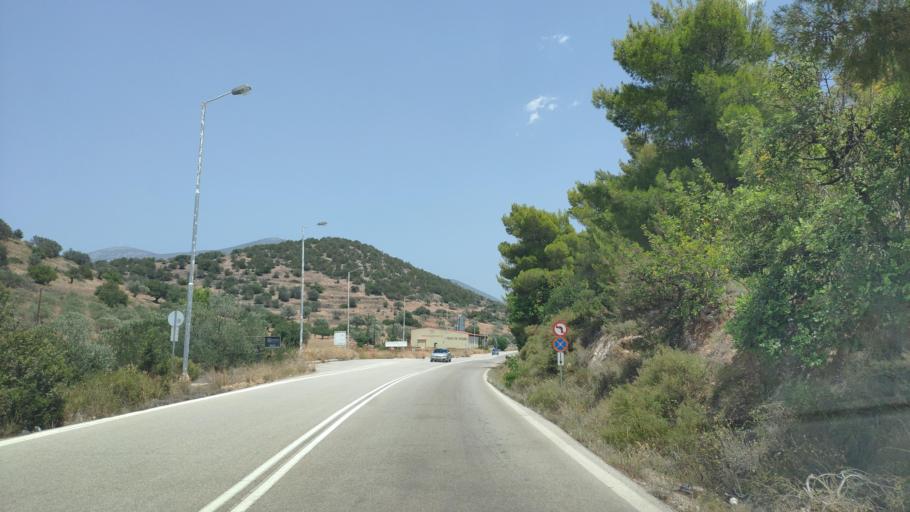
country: GR
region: Peloponnese
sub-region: Nomos Argolidos
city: Koilas
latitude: 37.4287
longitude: 23.1553
